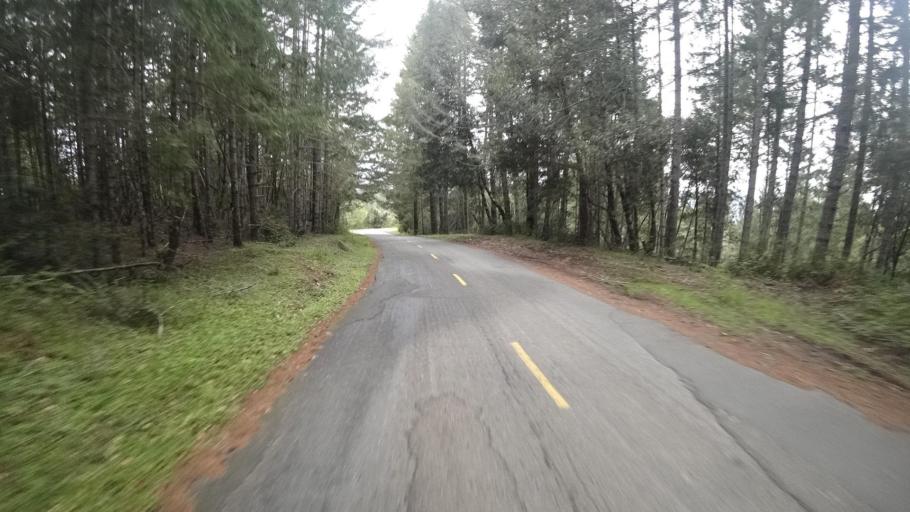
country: US
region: California
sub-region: Humboldt County
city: Redway
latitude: 40.2742
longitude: -123.7808
